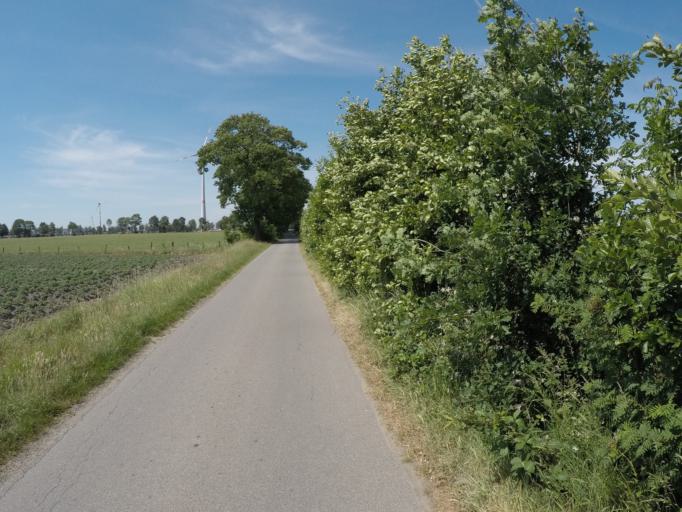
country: BE
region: Flanders
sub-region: Provincie Antwerpen
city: Hoogstraten
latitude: 51.4101
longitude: 4.7106
